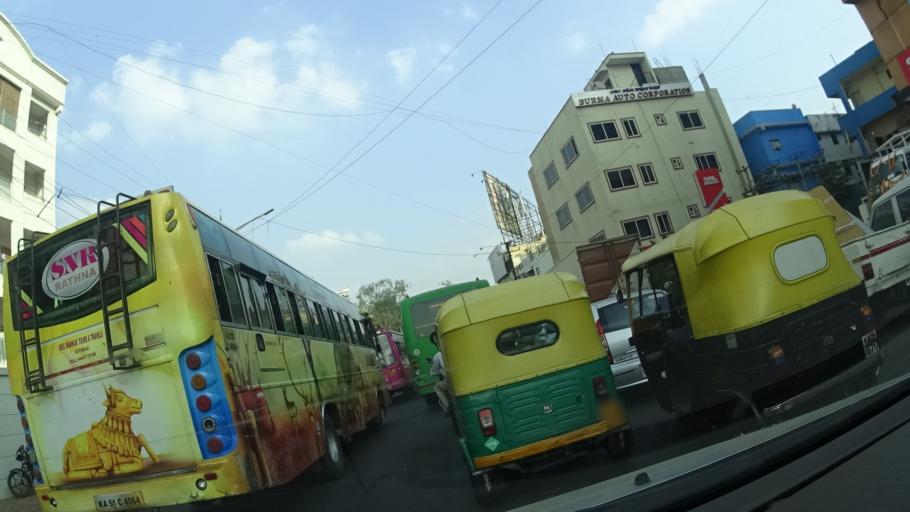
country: IN
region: Karnataka
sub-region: Bangalore Urban
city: Bangalore
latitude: 12.9559
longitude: 77.5848
